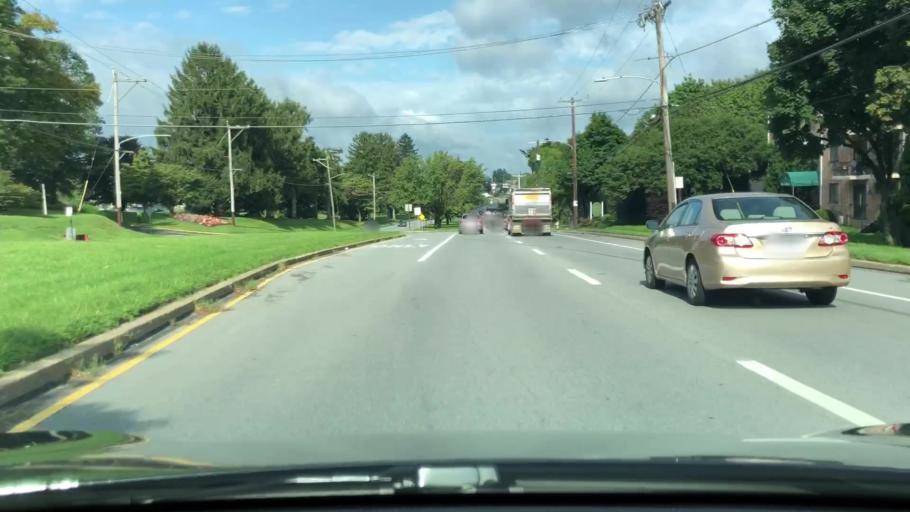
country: US
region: Pennsylvania
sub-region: Delaware County
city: Broomall
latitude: 39.9846
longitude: -75.3891
